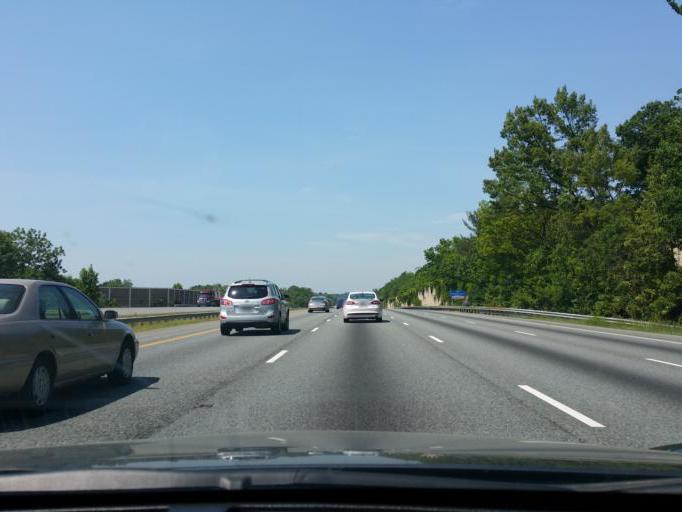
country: US
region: Maryland
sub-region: Howard County
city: West Elkridge
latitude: 39.2094
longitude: -76.7437
